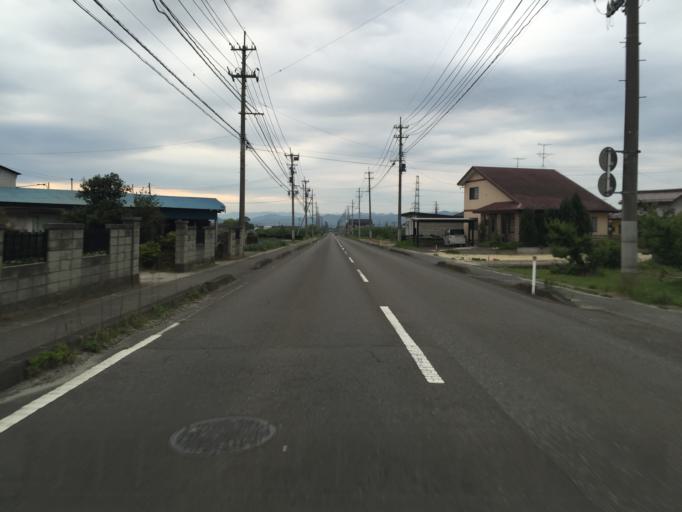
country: JP
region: Fukushima
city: Fukushima-shi
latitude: 37.8182
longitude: 140.4538
